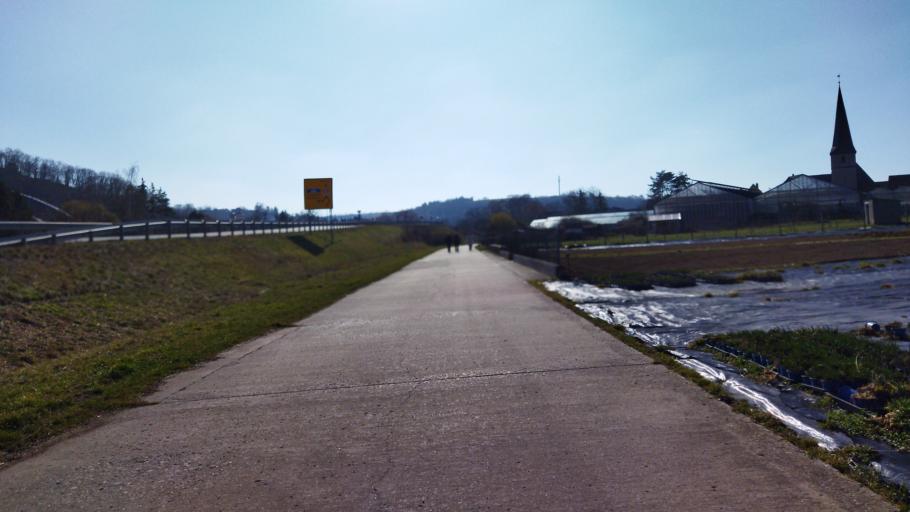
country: DE
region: Bavaria
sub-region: Regierungsbezirk Unterfranken
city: Segnitz
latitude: 49.6727
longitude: 10.1466
